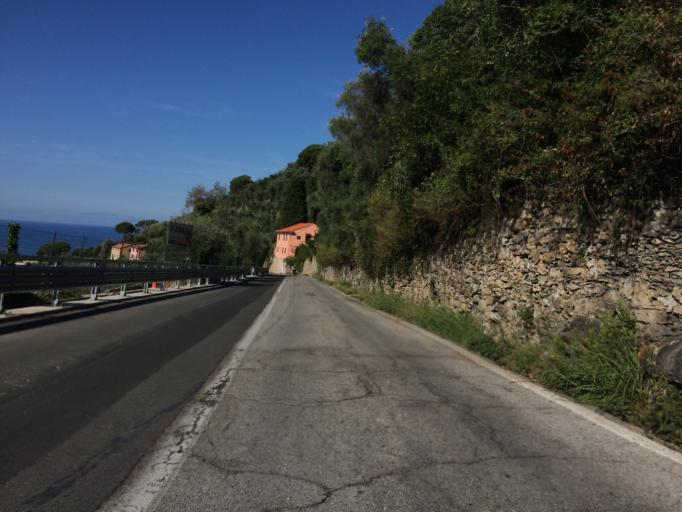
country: IT
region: Liguria
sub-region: Provincia di Genova
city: Zoagli
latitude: 44.3334
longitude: 9.2819
